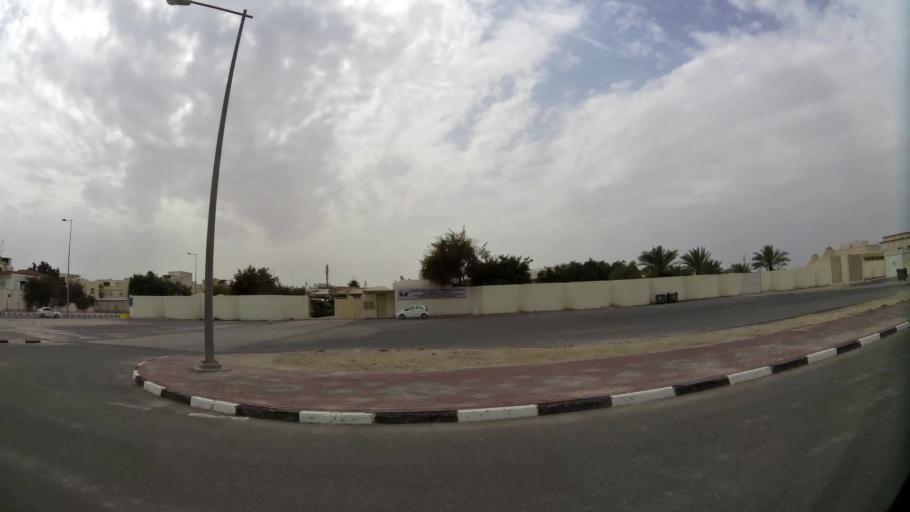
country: QA
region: Baladiyat ad Dawhah
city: Doha
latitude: 25.3360
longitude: 51.5030
